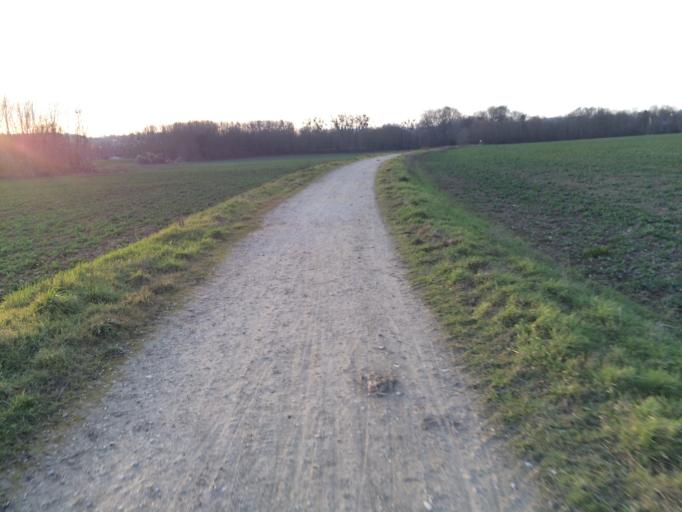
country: FR
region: Ile-de-France
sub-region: Departement de l'Essonne
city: Champlan
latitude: 48.7011
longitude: 2.2785
